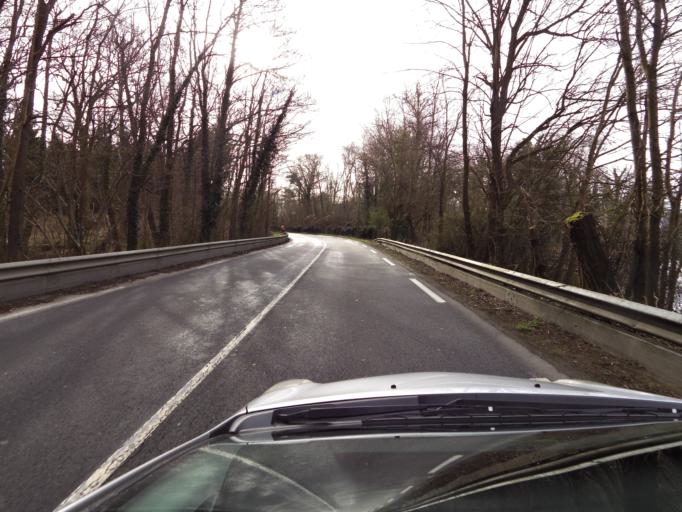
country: FR
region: Picardie
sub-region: Departement de l'Oise
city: Ver-sur-Launette
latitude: 49.1353
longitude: 2.6888
